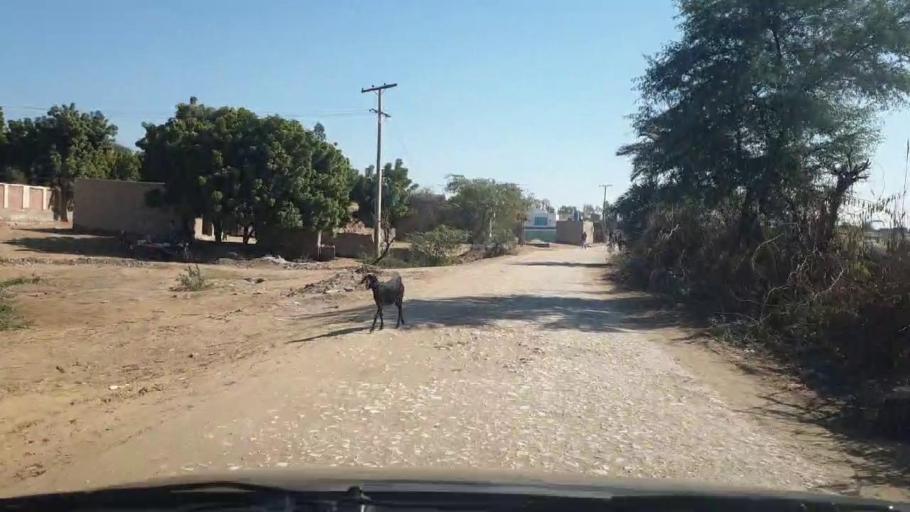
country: PK
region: Sindh
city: Bozdar
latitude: 27.0639
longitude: 68.6230
